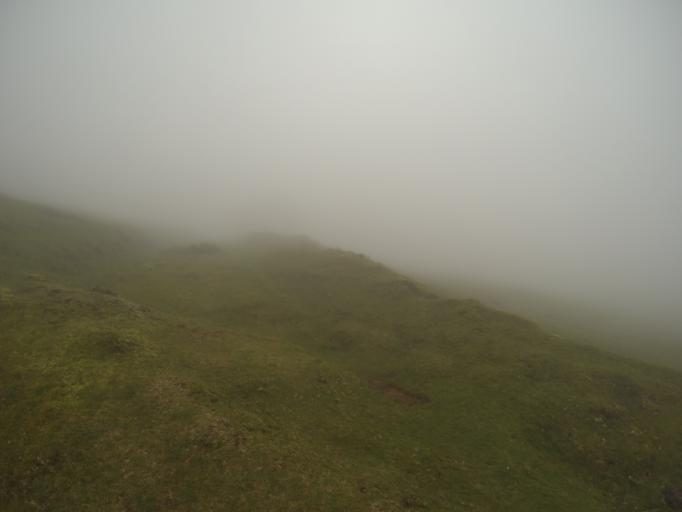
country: PT
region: Madeira
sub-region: Porto Moniz
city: Porto Moniz
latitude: 32.8123
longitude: -17.1434
